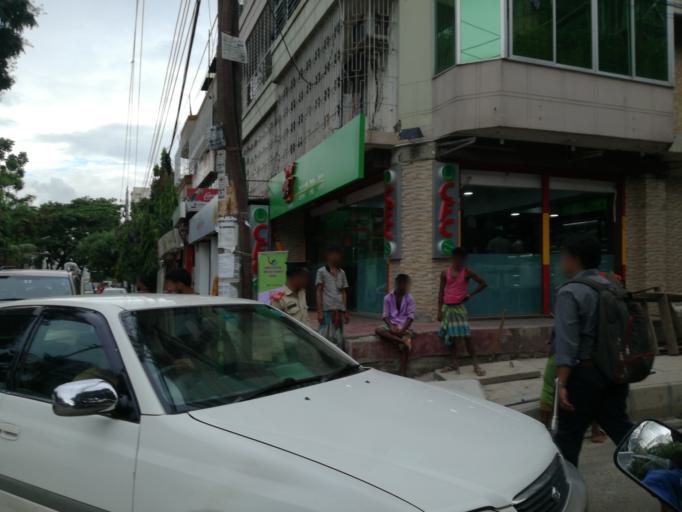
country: BD
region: Dhaka
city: Paltan
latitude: 23.7744
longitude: 90.4150
